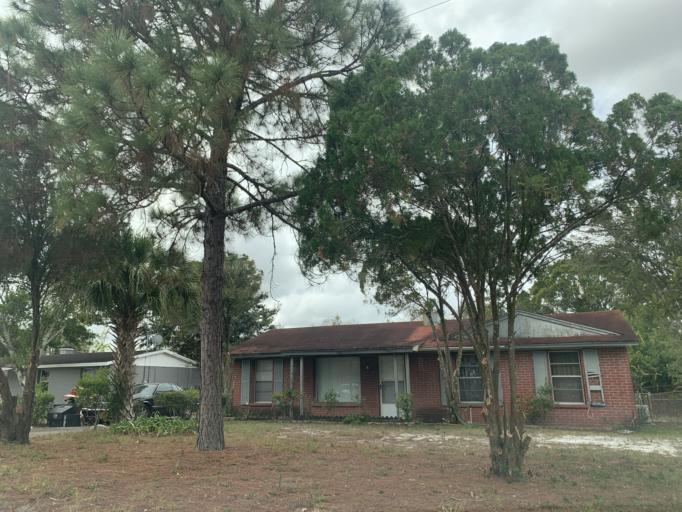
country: US
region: Florida
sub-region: Hillsborough County
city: East Lake-Orient Park
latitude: 27.9740
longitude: -82.4092
